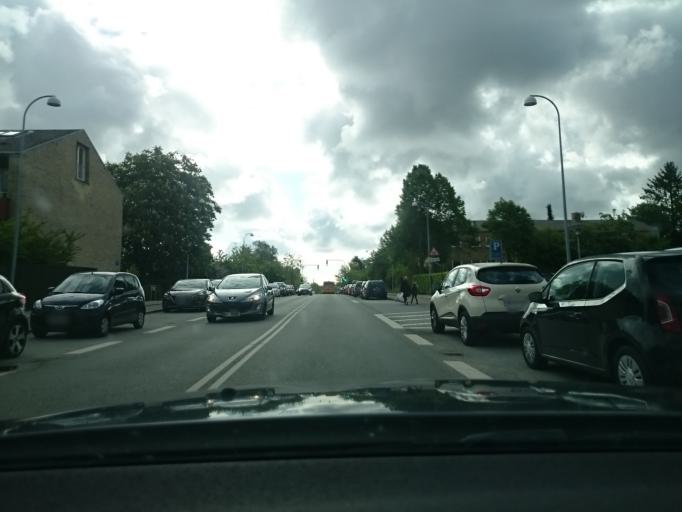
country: DK
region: Capital Region
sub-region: Gladsaxe Municipality
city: Buddinge
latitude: 55.7424
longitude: 12.5014
